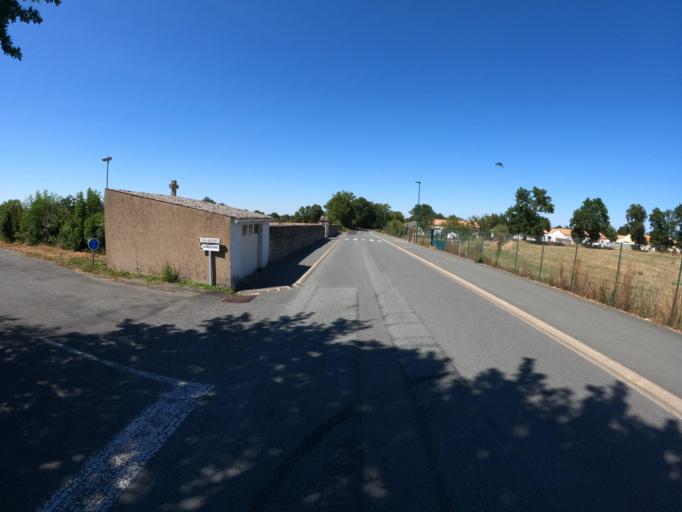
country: FR
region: Pays de la Loire
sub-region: Departement de la Vendee
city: Saint-Aubin-des-Ormeaux
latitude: 46.9754
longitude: -1.0519
